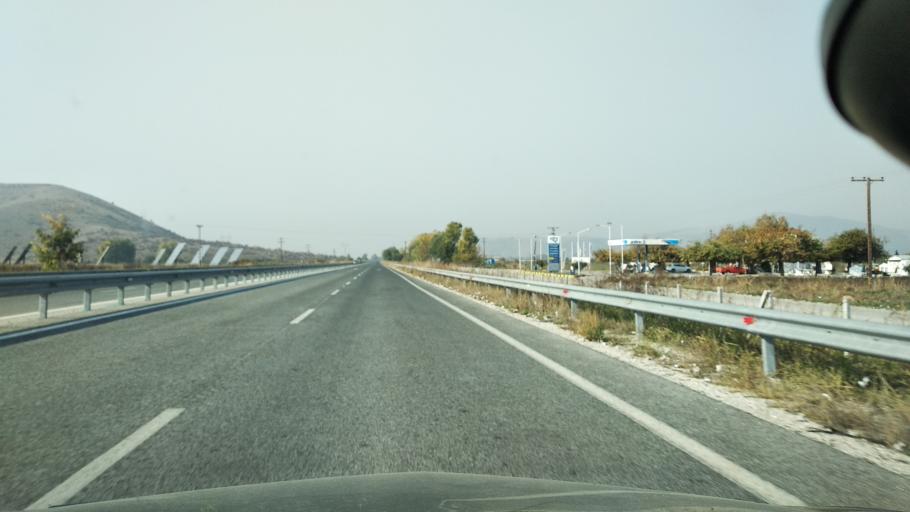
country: GR
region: Thessaly
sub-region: Trikala
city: Farkadona
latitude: 39.5836
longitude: 22.0346
